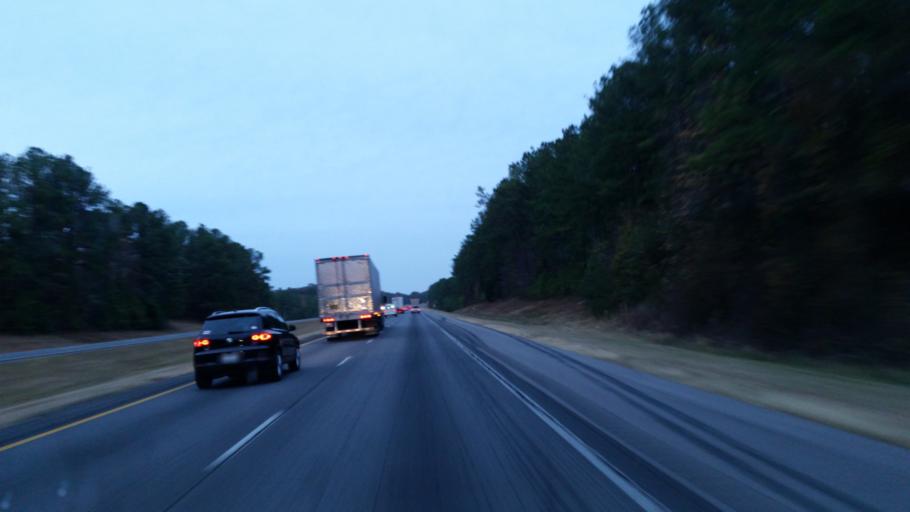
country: US
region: Alabama
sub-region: Hale County
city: Moundville
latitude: 33.0354
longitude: -87.7363
